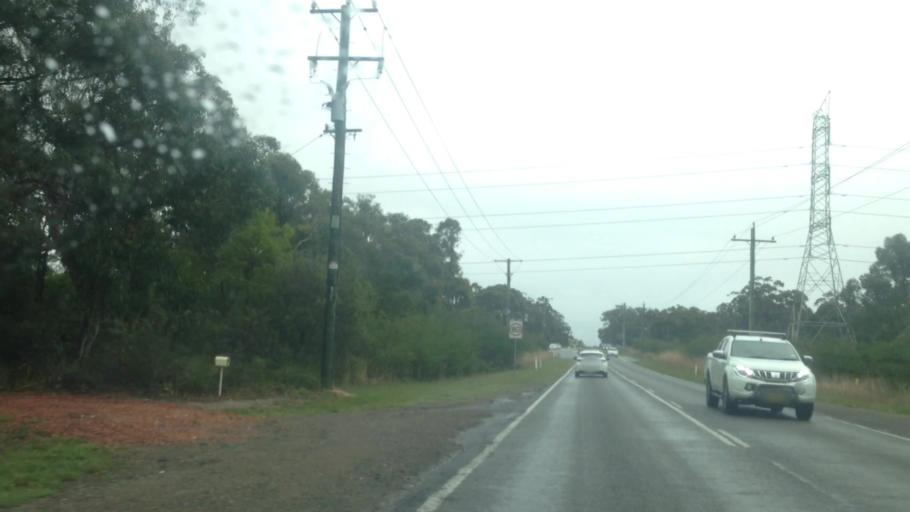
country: AU
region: New South Wales
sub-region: Wyong Shire
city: Charmhaven
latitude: -33.1591
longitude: 151.4786
